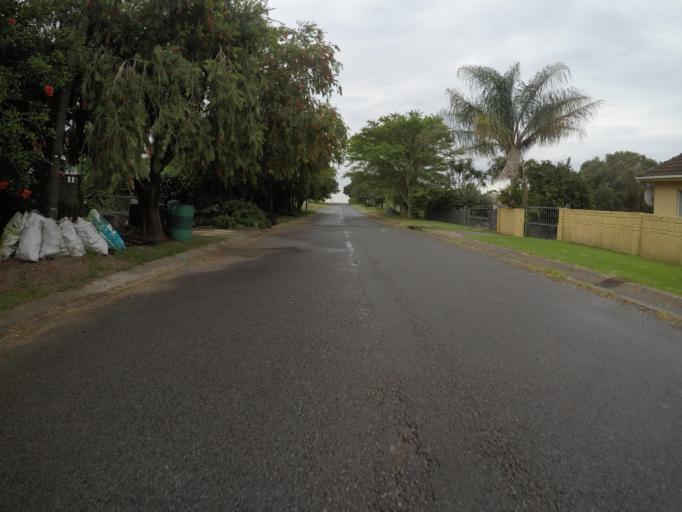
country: ZA
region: Eastern Cape
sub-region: Buffalo City Metropolitan Municipality
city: East London
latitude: -32.9654
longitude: 27.8448
